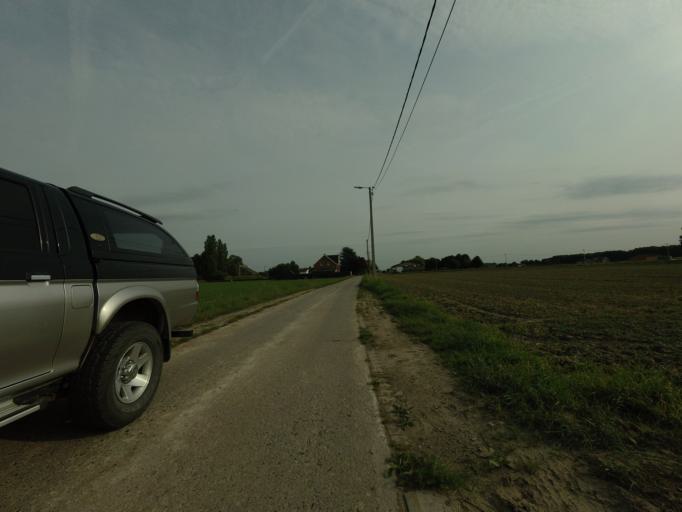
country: BE
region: Flanders
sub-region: Provincie Vlaams-Brabant
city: Kampenhout
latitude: 50.9448
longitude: 4.5375
